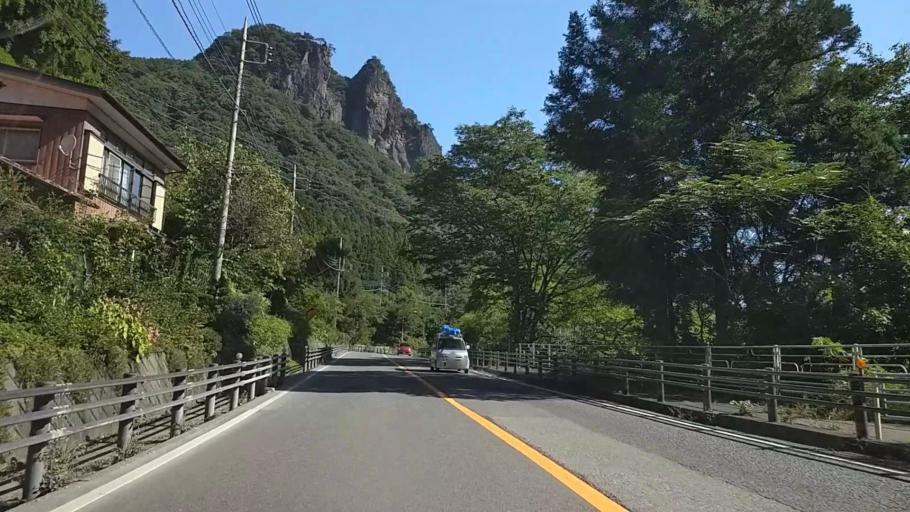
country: JP
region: Gunma
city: Annaka
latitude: 36.3264
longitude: 138.7063
